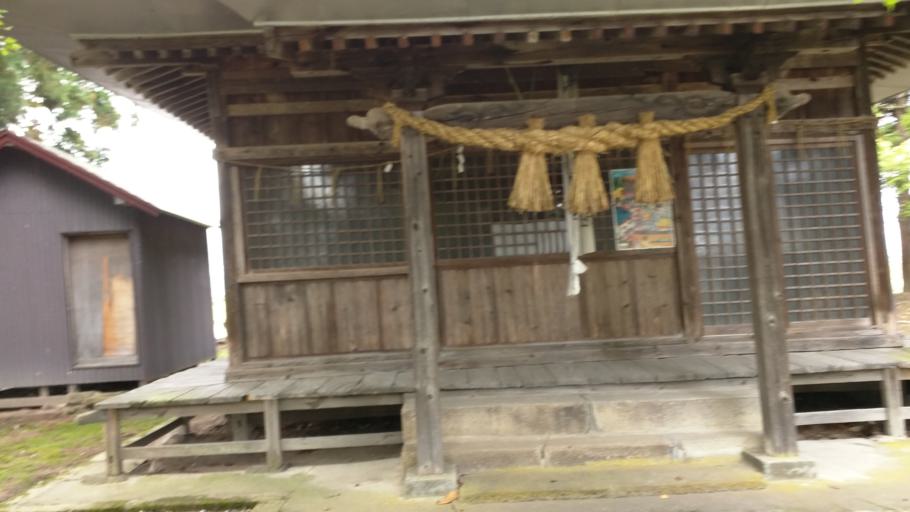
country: JP
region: Fukushima
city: Kitakata
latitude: 37.5283
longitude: 139.9079
